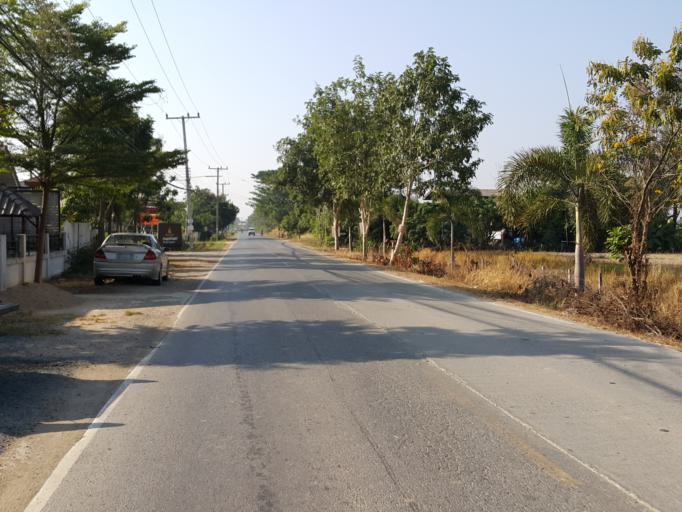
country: TH
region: Chiang Mai
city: San Kamphaeng
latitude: 18.7134
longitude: 99.1099
